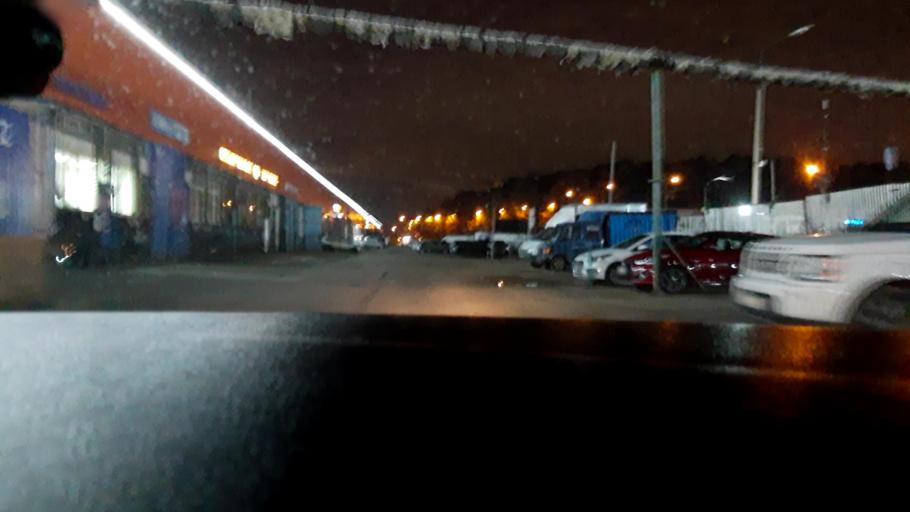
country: RU
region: Moscow
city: Annino
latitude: 55.5804
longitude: 37.5920
